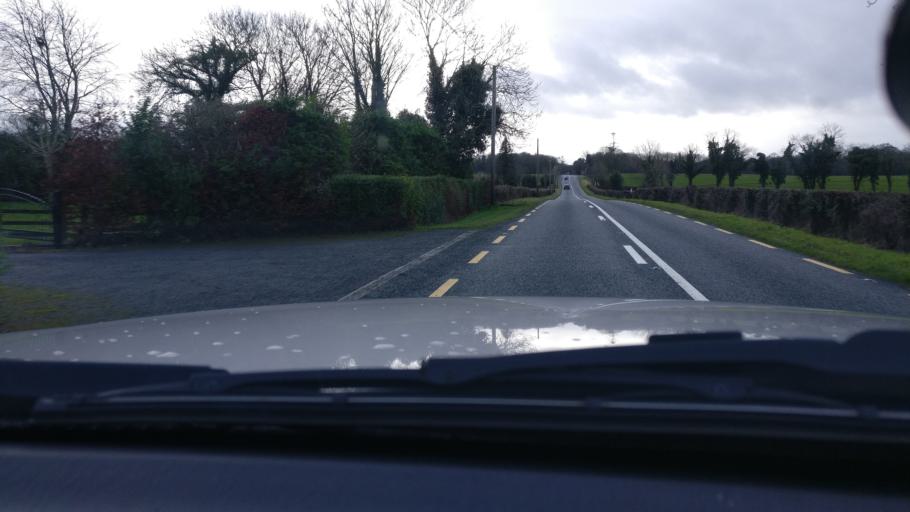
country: IE
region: Leinster
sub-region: An Iarmhi
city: Moate
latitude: 53.5987
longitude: -7.7146
